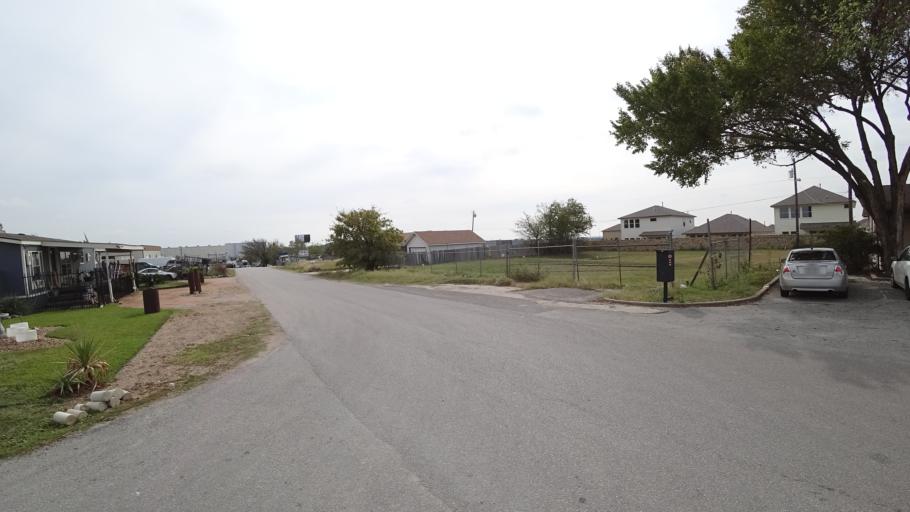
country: US
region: Texas
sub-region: Travis County
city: Wells Branch
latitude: 30.4480
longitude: -97.6698
